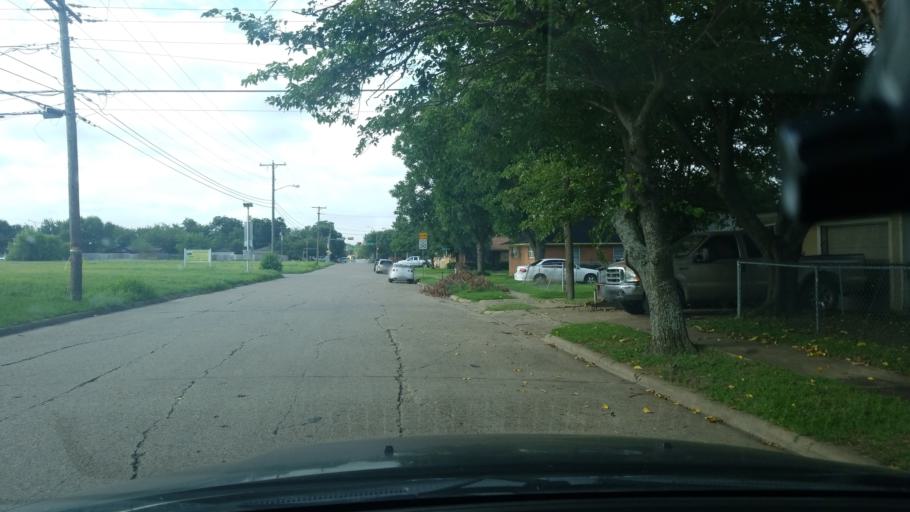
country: US
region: Texas
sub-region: Dallas County
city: Balch Springs
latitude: 32.7505
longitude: -96.6699
